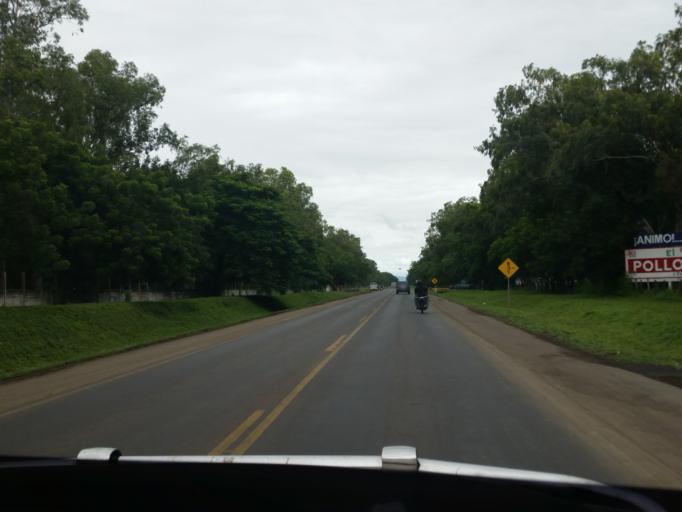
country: NI
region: Managua
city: Tipitapa
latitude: 12.2079
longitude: -86.1006
